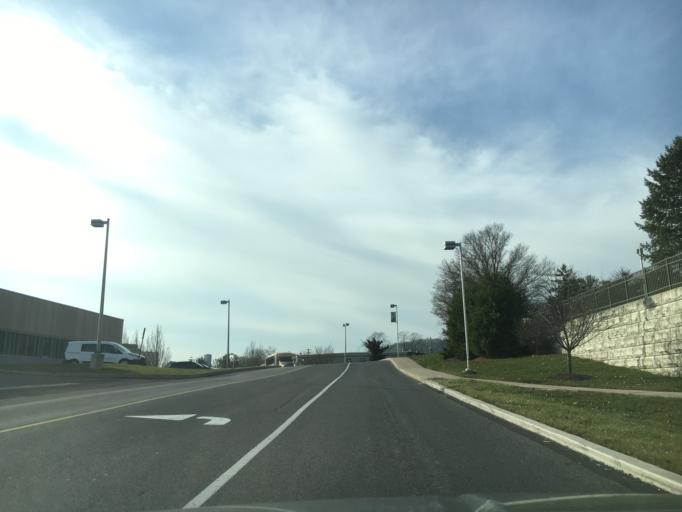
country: US
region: Pennsylvania
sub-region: Montour County
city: Danville
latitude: 40.9698
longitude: -76.6037
